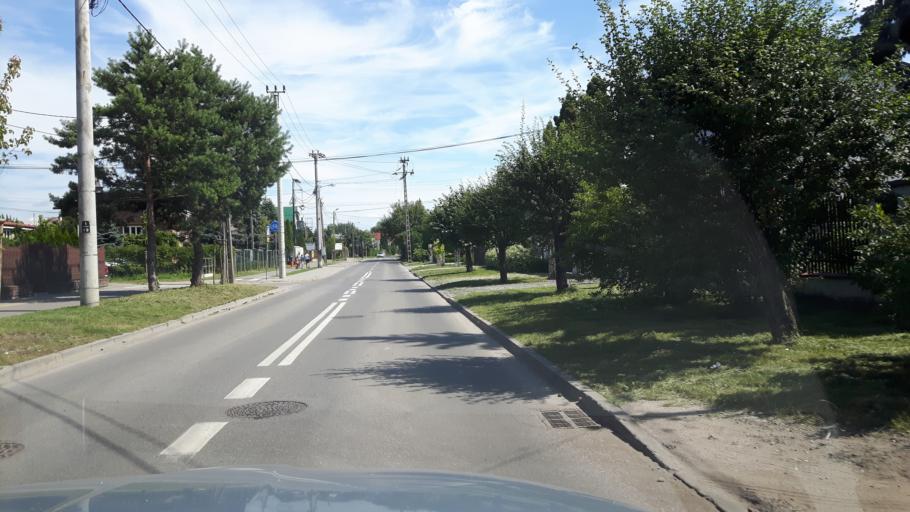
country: PL
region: Masovian Voivodeship
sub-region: Powiat wolominski
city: Marki
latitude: 52.3149
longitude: 21.1094
